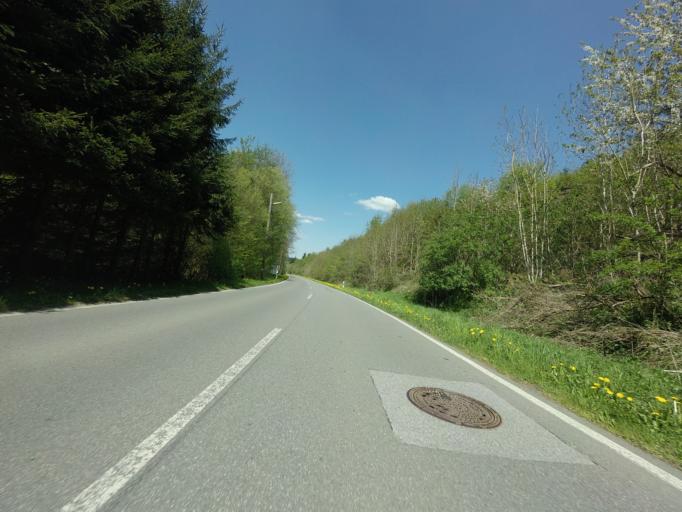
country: DE
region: North Rhine-Westphalia
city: Hemer
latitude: 51.3666
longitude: 7.7870
